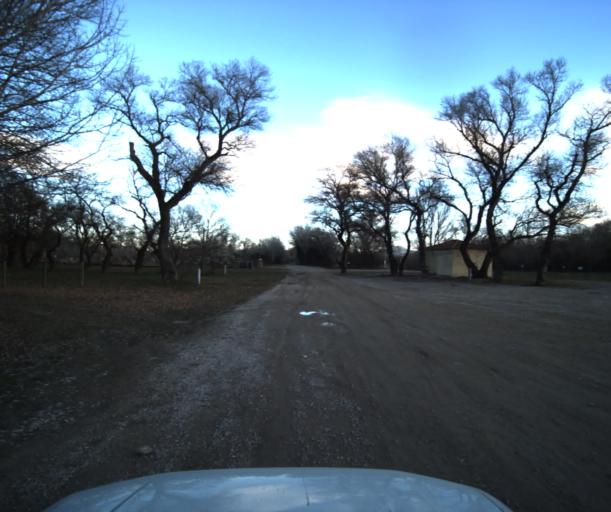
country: FR
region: Provence-Alpes-Cote d'Azur
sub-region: Departement du Vaucluse
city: Pertuis
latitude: 43.6696
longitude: 5.5002
